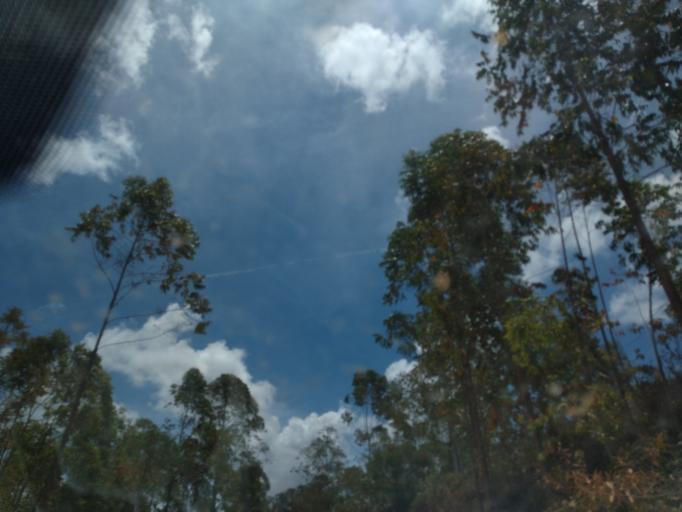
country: BR
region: Minas Gerais
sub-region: Tiradentes
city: Tiradentes
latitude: -20.9062
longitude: -44.2850
